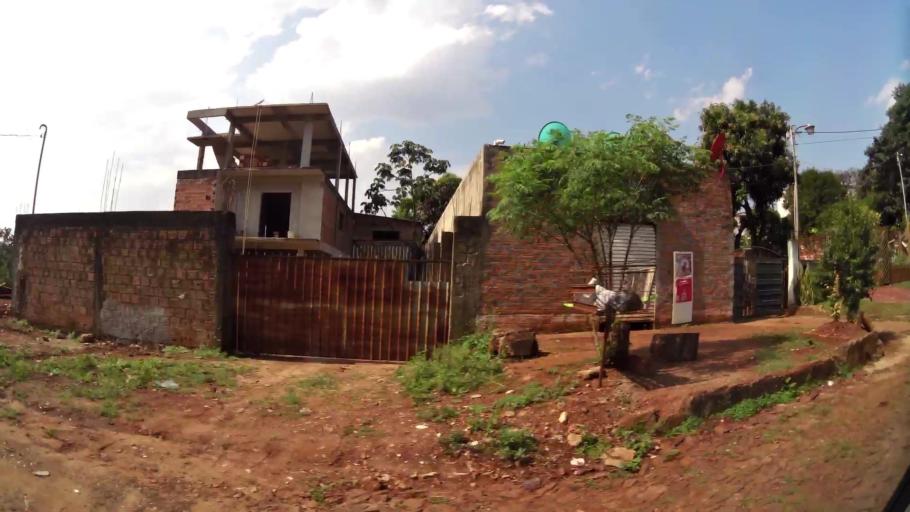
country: PY
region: Alto Parana
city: Ciudad del Este
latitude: -25.5073
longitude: -54.6256
